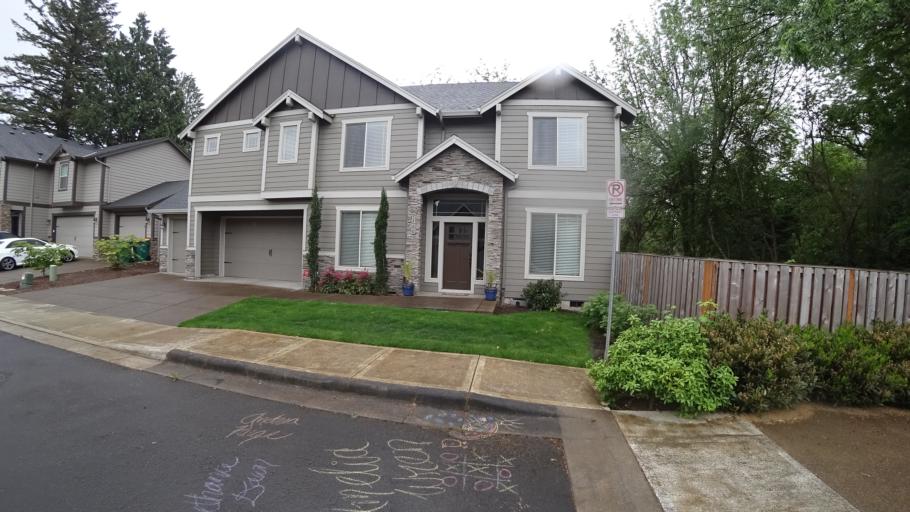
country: US
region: Oregon
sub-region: Washington County
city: Garden Home-Whitford
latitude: 45.4680
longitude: -122.7722
